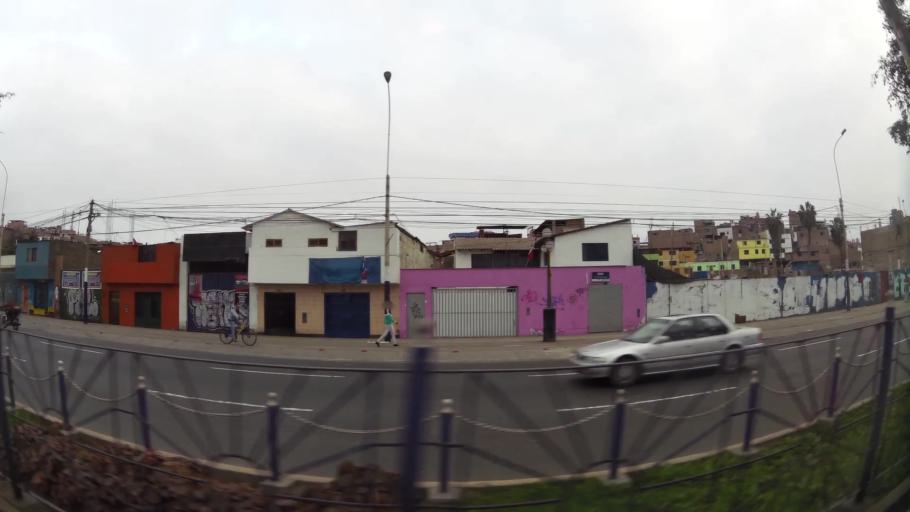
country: PE
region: Lima
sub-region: Lima
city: Surco
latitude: -12.1840
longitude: -77.0043
